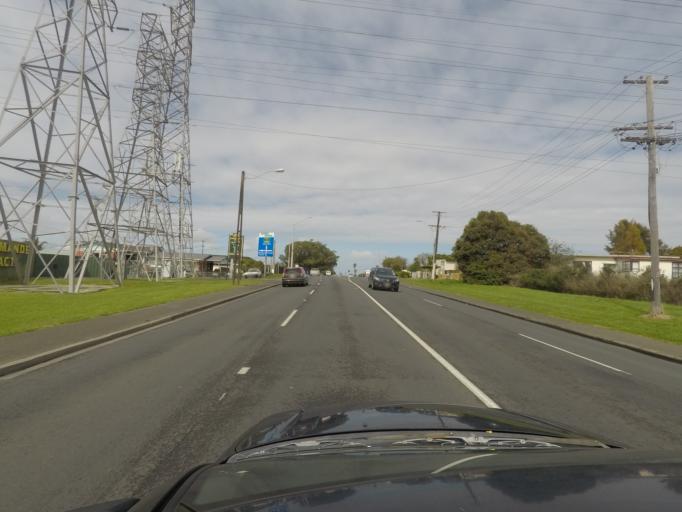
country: NZ
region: Auckland
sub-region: Auckland
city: Tamaki
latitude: -36.9068
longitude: 174.8399
